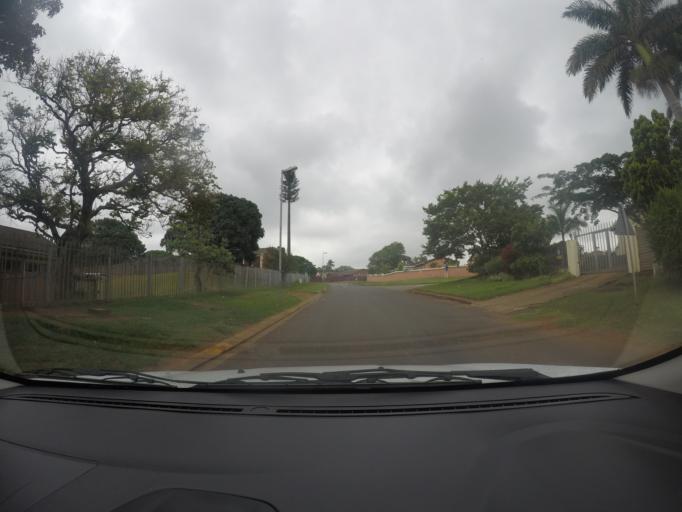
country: ZA
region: KwaZulu-Natal
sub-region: uThungulu District Municipality
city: Empangeni
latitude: -28.7678
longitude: 31.8979
